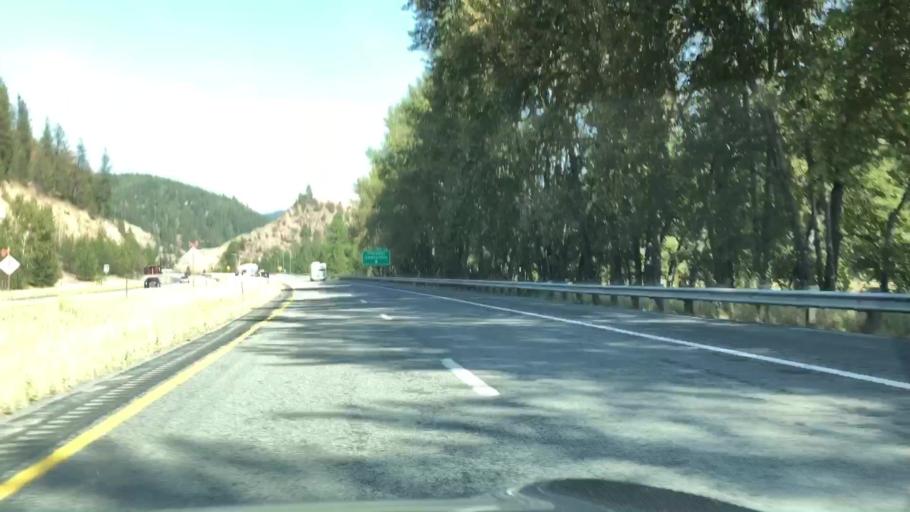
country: US
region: Idaho
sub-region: Shoshone County
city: Pinehurst
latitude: 47.5434
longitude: -116.2349
